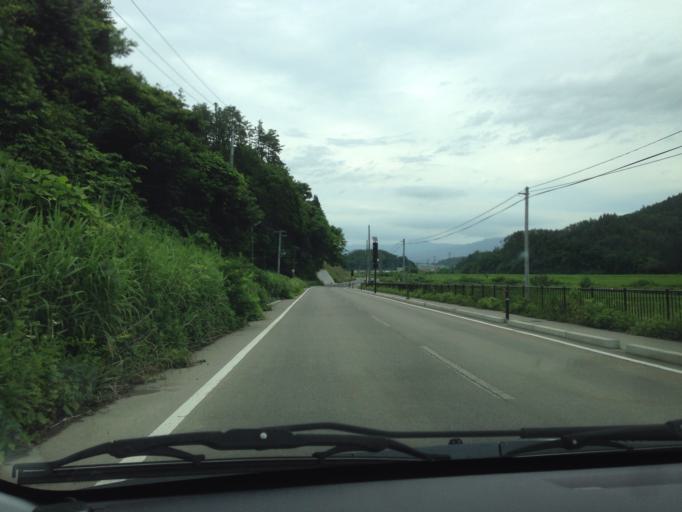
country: JP
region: Fukushima
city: Kitakata
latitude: 37.4154
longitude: 139.8754
